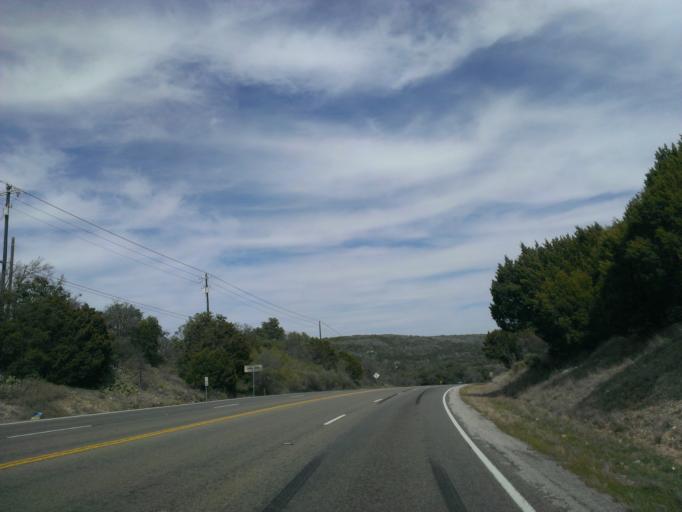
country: US
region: Texas
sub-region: Llano County
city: Kingsland
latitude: 30.6329
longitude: -98.4096
